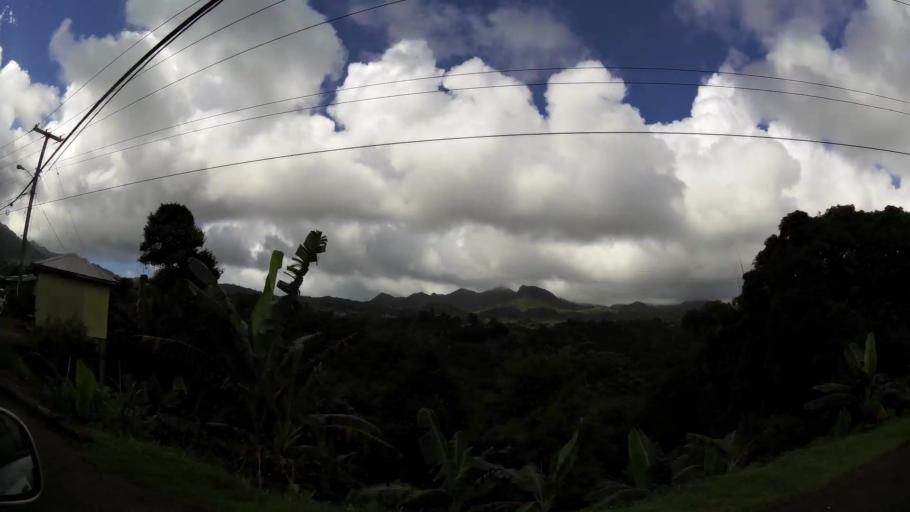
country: GD
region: Saint Andrew
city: Grenville
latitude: 12.1197
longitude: -61.6698
